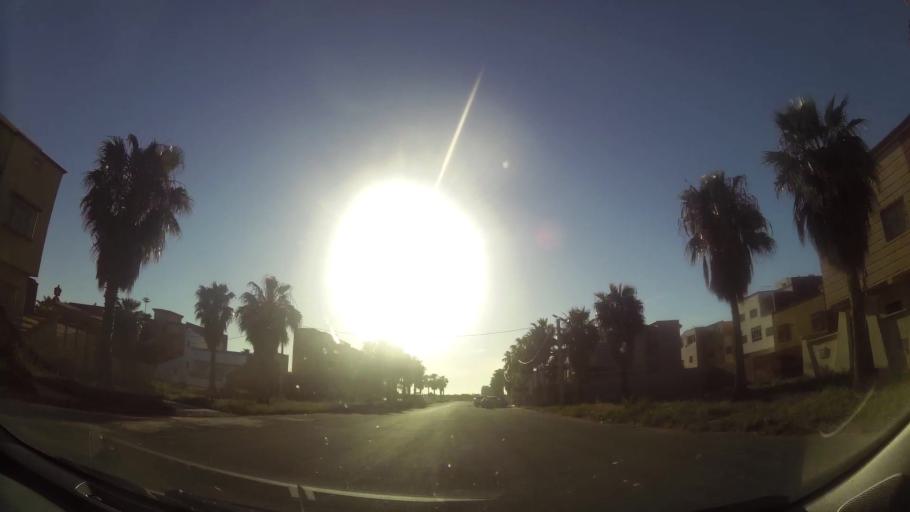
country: MA
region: Oriental
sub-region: Berkane-Taourirt
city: Madagh
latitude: 35.0829
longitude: -2.2468
